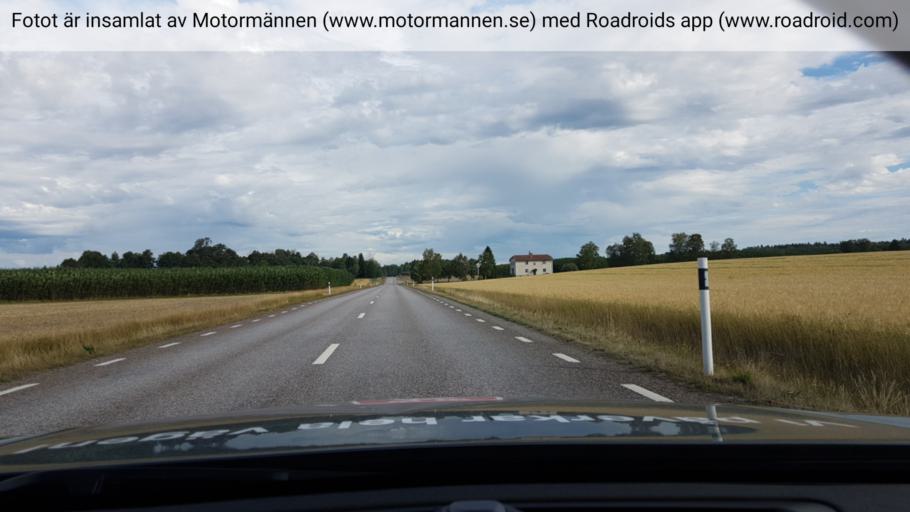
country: SE
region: Uppsala
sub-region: Heby Kommun
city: Morgongava
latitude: 59.8324
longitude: 16.9267
